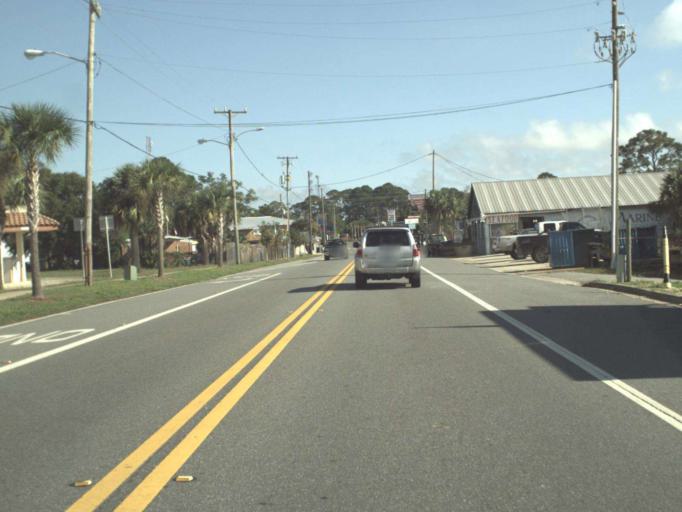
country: US
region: Florida
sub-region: Franklin County
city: Carrabelle
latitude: 29.8521
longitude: -84.6667
